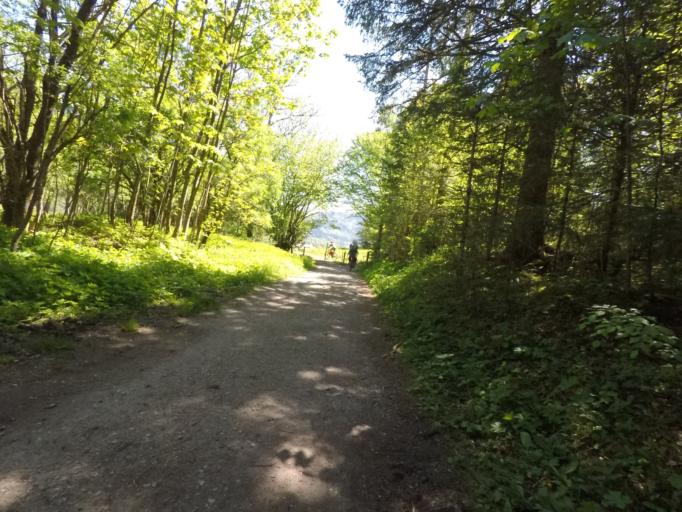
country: DE
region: Bavaria
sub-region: Upper Bavaria
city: Bayrischzell
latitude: 47.6776
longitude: 11.9897
